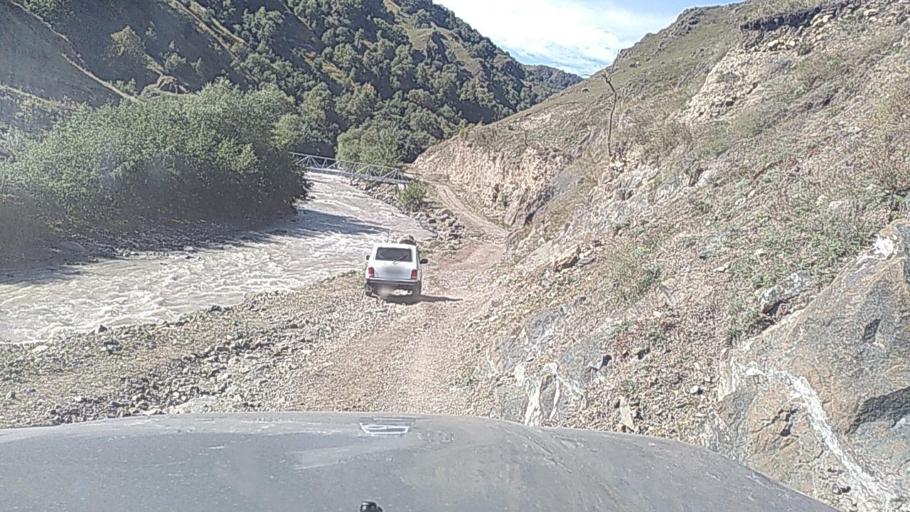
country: RU
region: Kabardino-Balkariya
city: Kamennomostskoye
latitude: 43.7231
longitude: 42.9030
